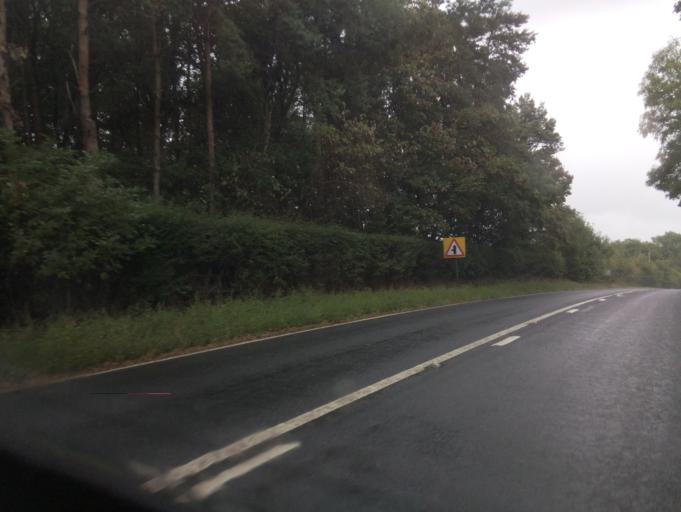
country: GB
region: England
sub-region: North Yorkshire
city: Pannal
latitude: 53.9296
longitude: -1.5367
